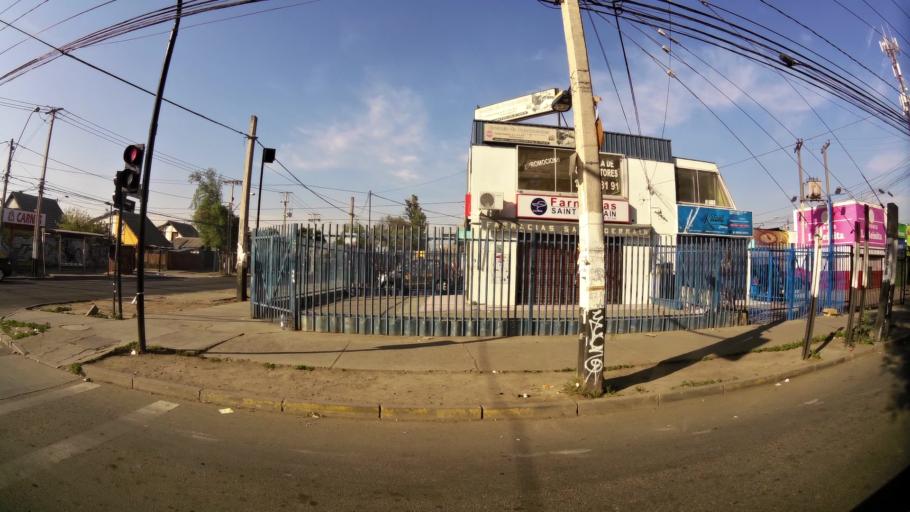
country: CL
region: Santiago Metropolitan
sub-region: Provincia de Santiago
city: Lo Prado
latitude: -33.4701
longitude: -70.7483
